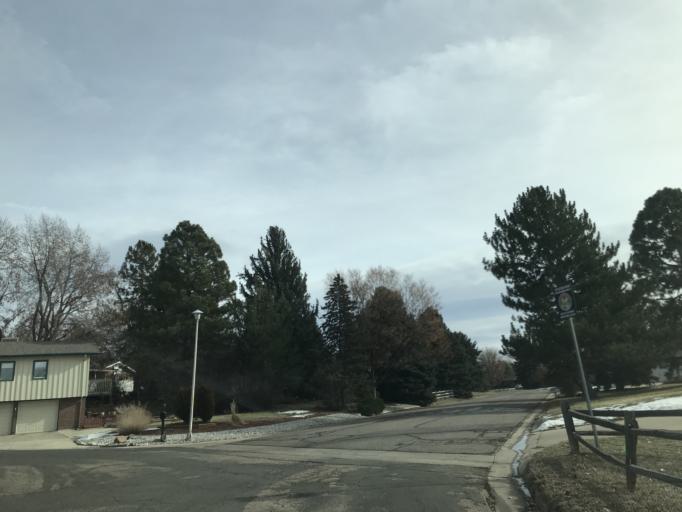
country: US
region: Colorado
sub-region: Arapahoe County
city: Littleton
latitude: 39.5963
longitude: -105.0143
